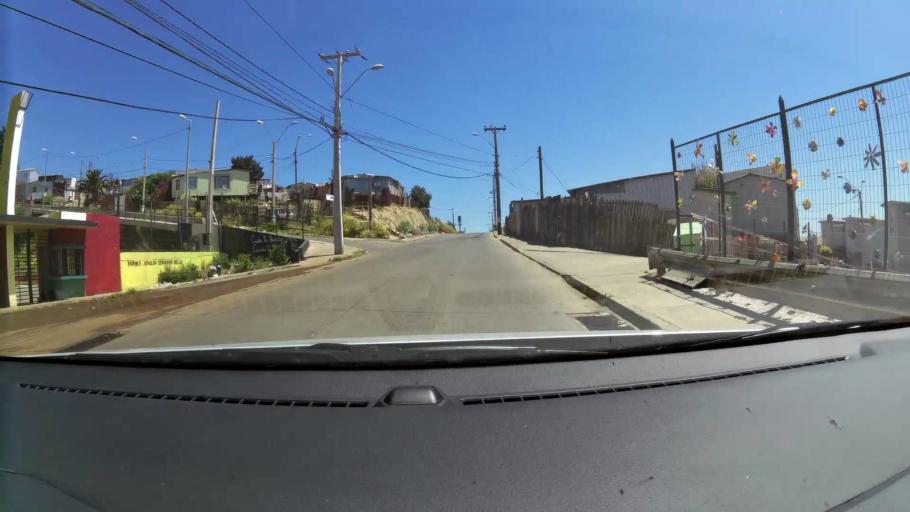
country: CL
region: Valparaiso
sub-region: Provincia de Valparaiso
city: Valparaiso
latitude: -33.0586
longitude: -71.6393
